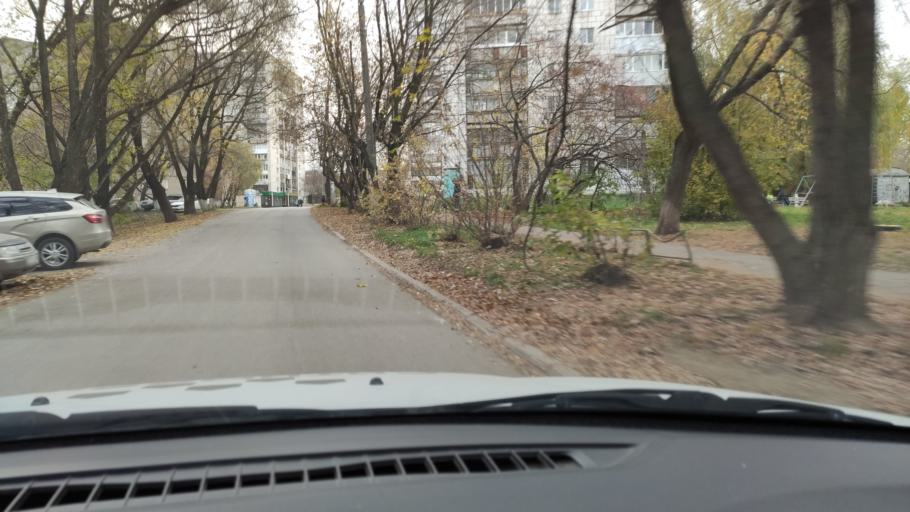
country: RU
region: Perm
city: Perm
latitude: 57.9805
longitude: 56.2323
